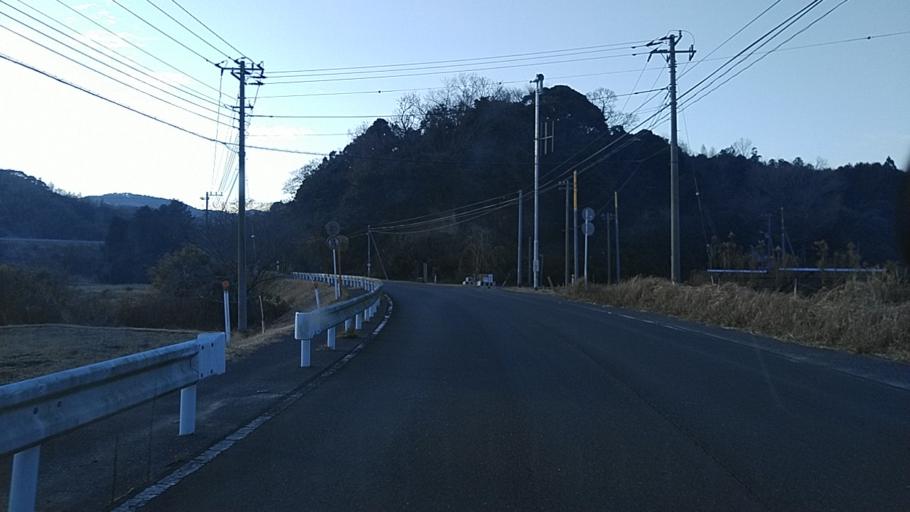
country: JP
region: Chiba
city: Kimitsu
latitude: 35.2817
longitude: 139.9232
